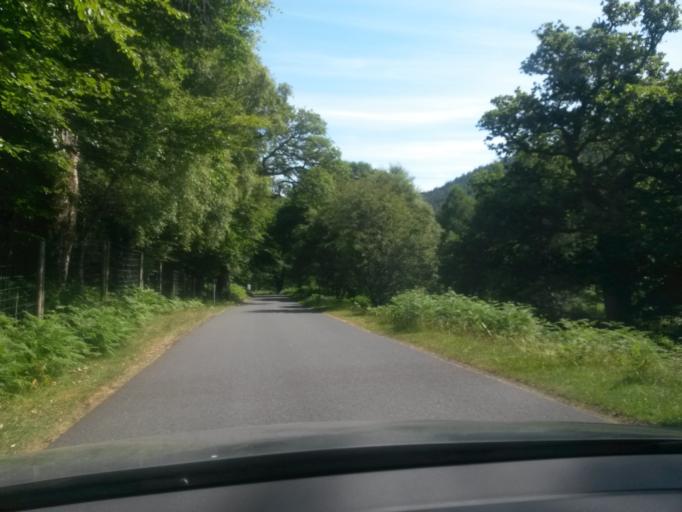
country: IE
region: Leinster
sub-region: Wicklow
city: Enniskerry
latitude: 53.1516
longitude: -6.2012
